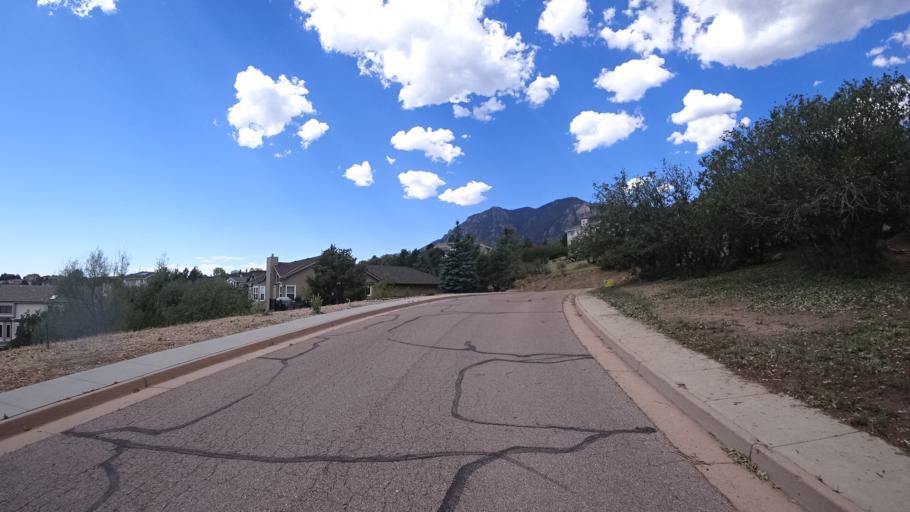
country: US
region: Colorado
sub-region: El Paso County
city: Fort Carson
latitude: 38.7630
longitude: -104.8217
